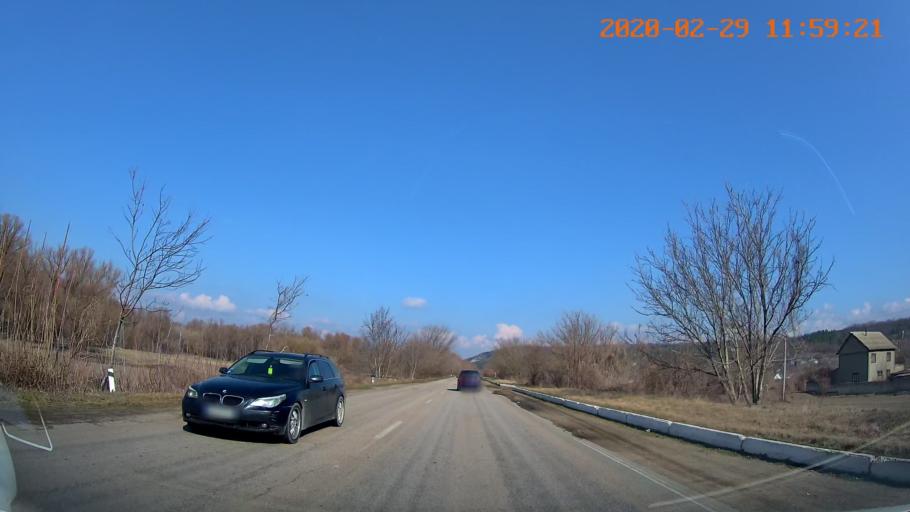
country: MD
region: Telenesti
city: Ribnita
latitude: 47.8241
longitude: 29.0165
